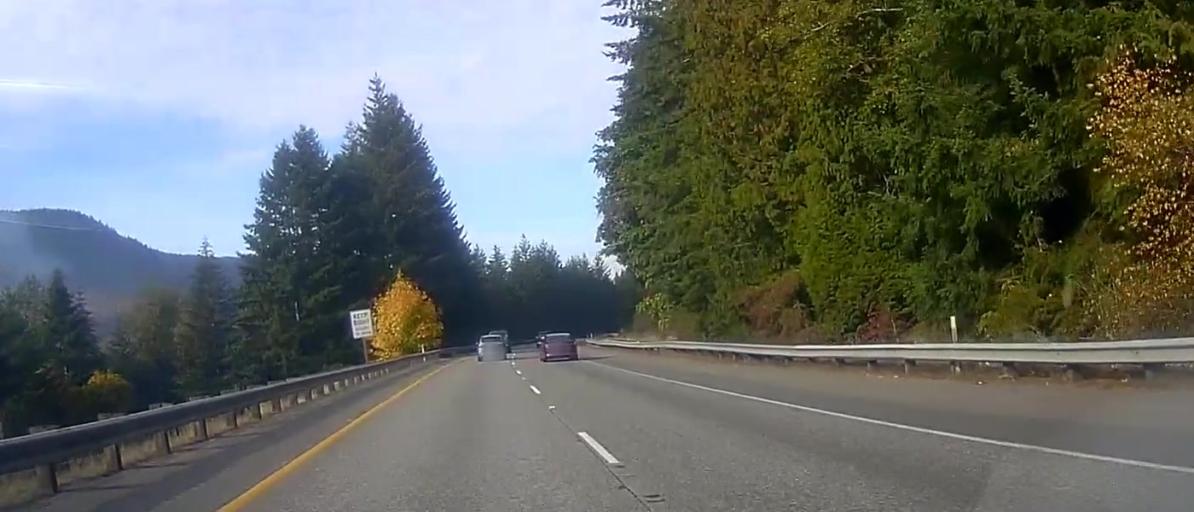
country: US
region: Washington
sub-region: Whatcom County
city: Geneva
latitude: 48.6891
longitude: -122.4232
